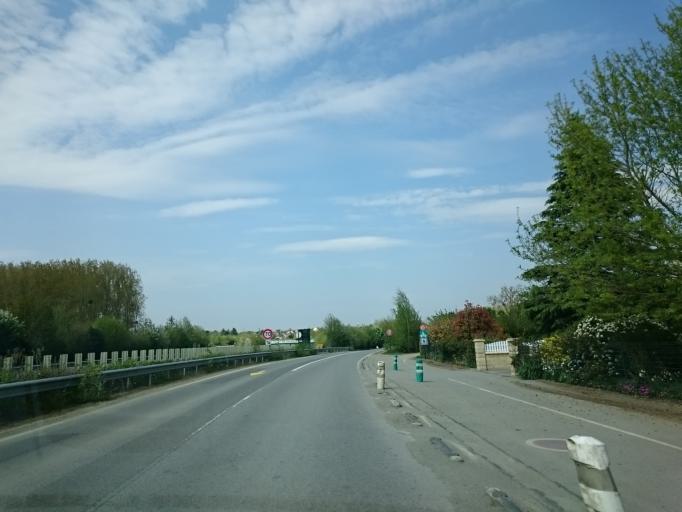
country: FR
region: Brittany
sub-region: Departement d'Ille-et-Vilaine
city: Vern-sur-Seiche
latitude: 48.0328
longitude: -1.5999
